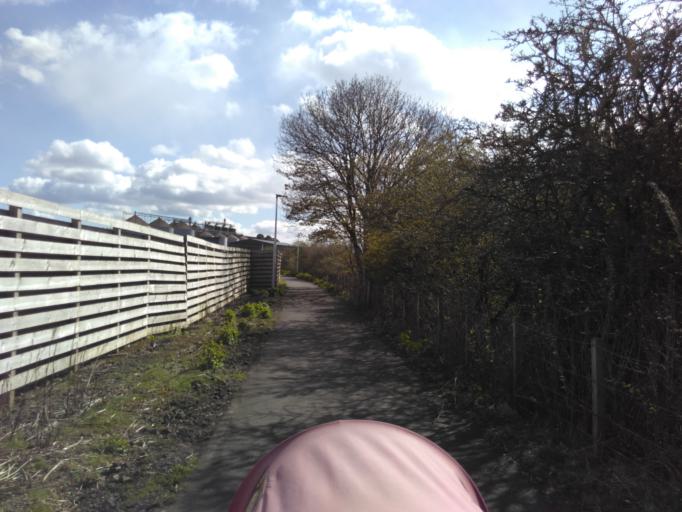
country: GB
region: Scotland
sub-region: Midlothian
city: Loanhead
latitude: 55.8884
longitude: -3.1473
